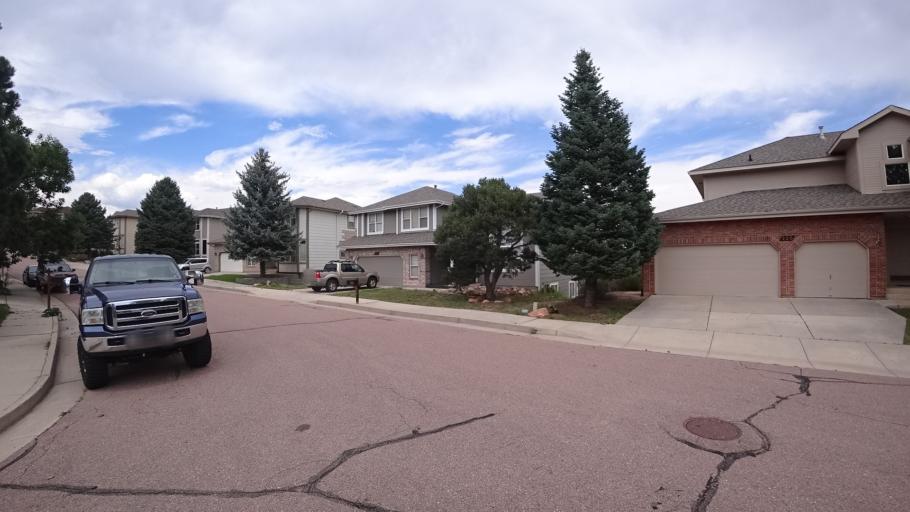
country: US
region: Colorado
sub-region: El Paso County
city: Colorado Springs
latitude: 38.9055
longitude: -104.8321
